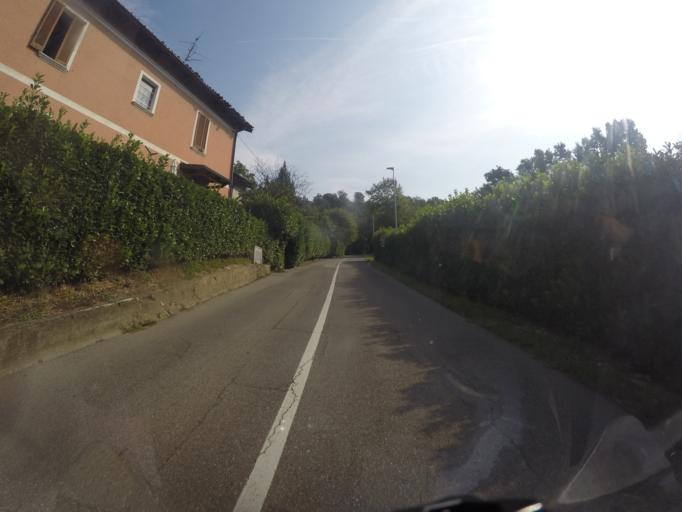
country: IT
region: Lombardy
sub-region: Provincia di Lecco
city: Santa Maria Hoe
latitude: 45.7428
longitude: 9.3877
